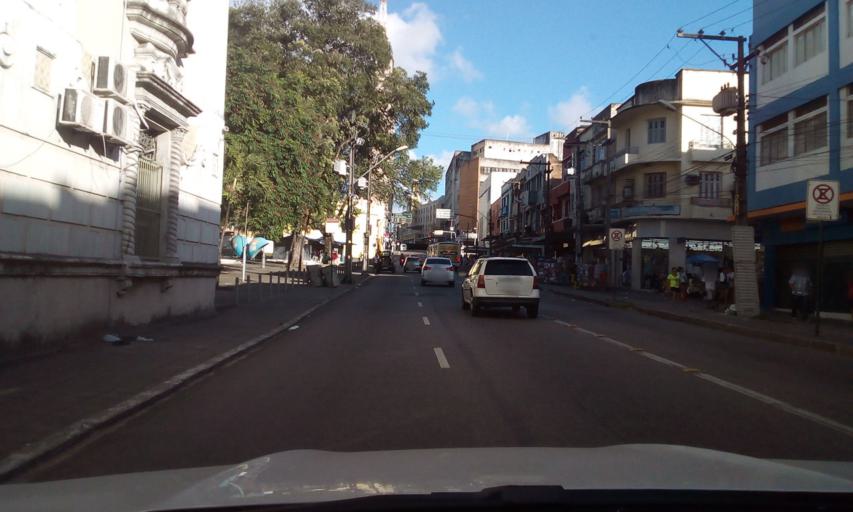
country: BR
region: Paraiba
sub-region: Joao Pessoa
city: Joao Pessoa
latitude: -7.1189
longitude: -34.8862
